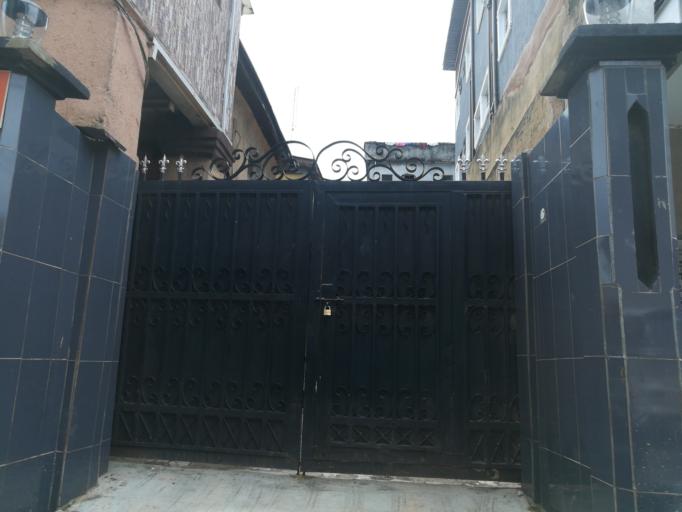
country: NG
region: Lagos
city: Lagos
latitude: 6.4573
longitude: 3.3816
